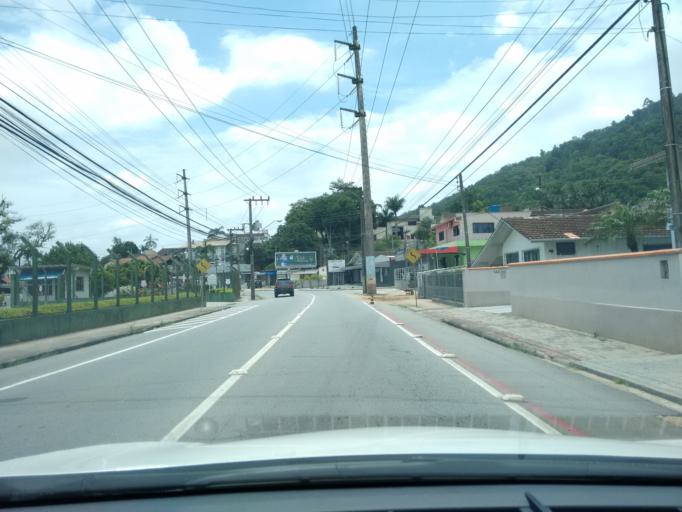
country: BR
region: Santa Catarina
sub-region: Jaragua Do Sul
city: Jaragua do Sul
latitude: -26.4942
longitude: -49.0691
